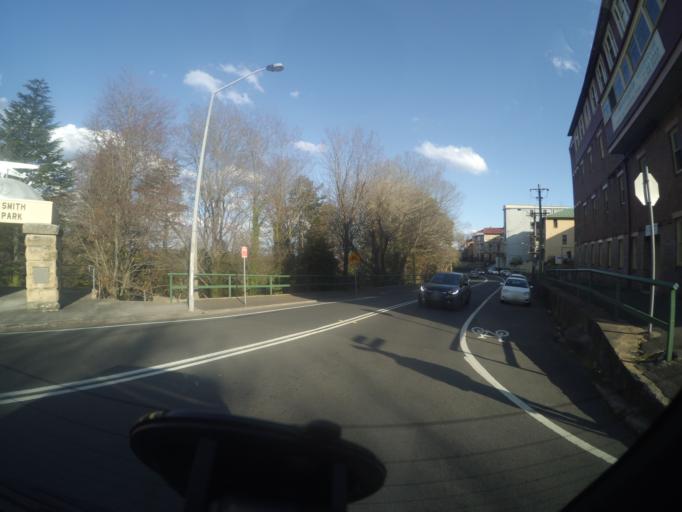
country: AU
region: New South Wales
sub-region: Blue Mountains Municipality
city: Katoomba
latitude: -33.7124
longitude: 150.3127
